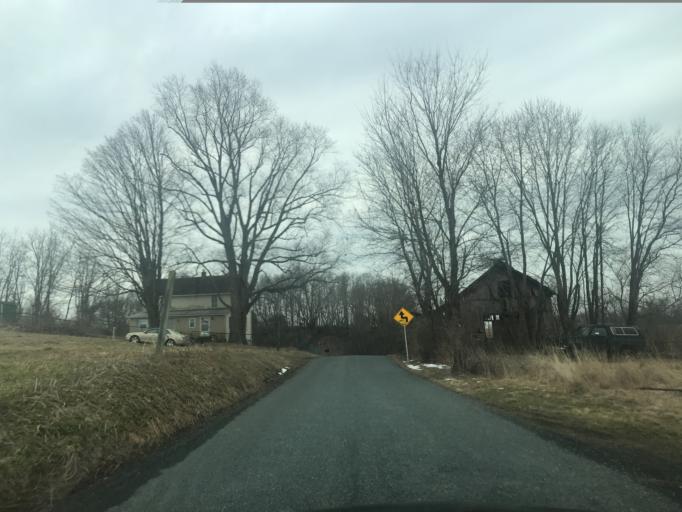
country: US
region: Maryland
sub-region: Harford County
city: Jarrettsville
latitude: 39.6755
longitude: -76.4168
